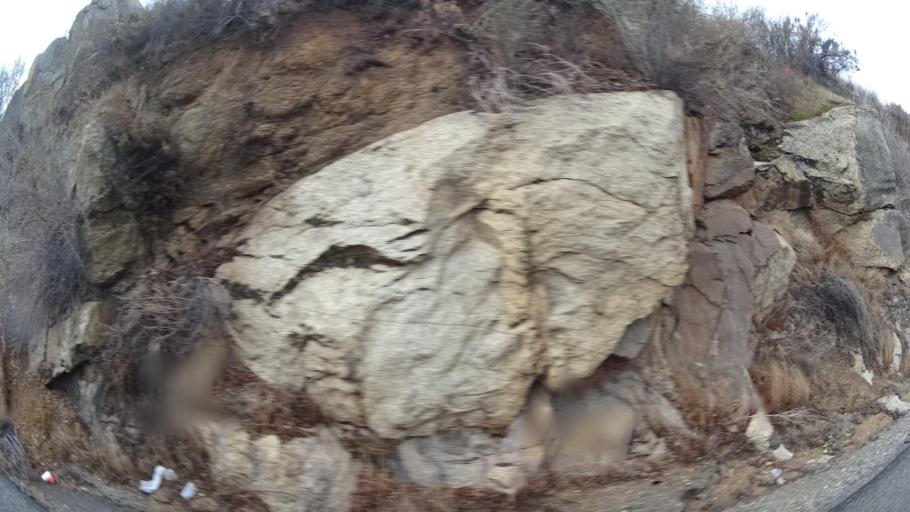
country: MX
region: Baja California
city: Tecate
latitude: 32.6014
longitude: -116.6351
